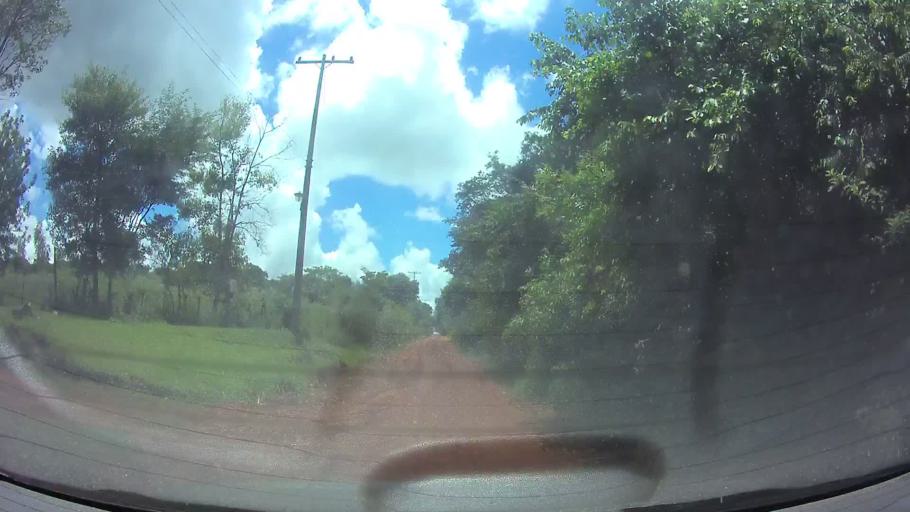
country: PY
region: Paraguari
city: La Colmena
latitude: -25.9486
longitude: -56.7820
